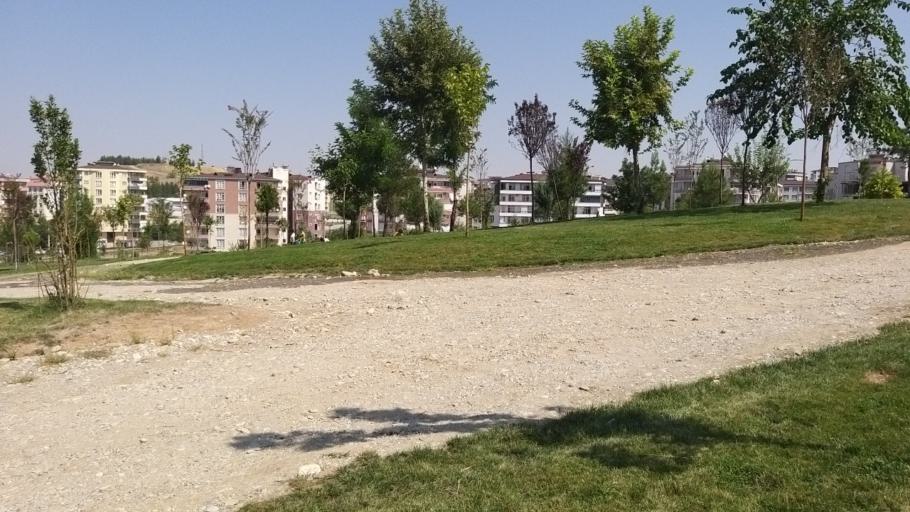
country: TR
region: Batman
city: Demiryol
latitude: 37.9070
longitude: 41.1454
